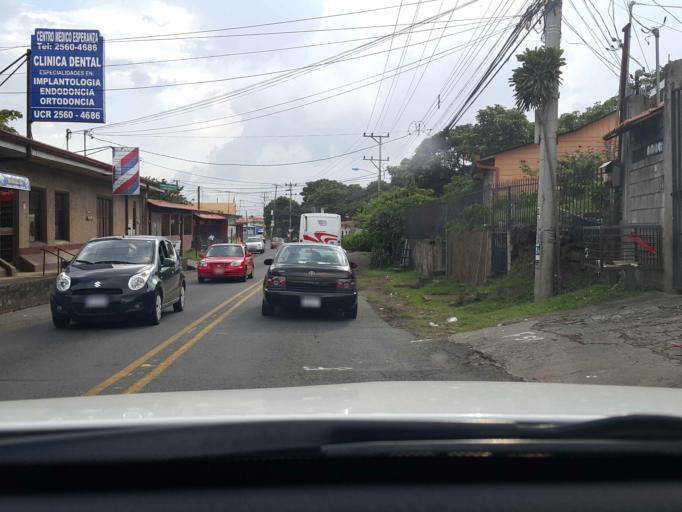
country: CR
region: Heredia
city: San Pablo
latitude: 10.0023
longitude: -84.0947
